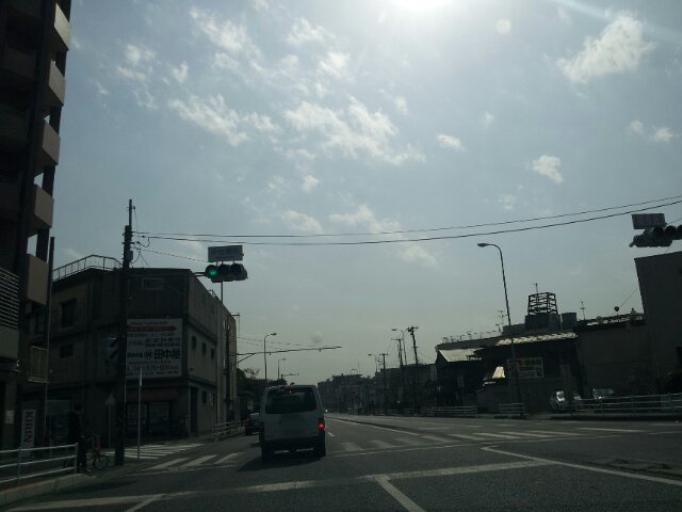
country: JP
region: Kanagawa
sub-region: Kawasaki-shi
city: Kawasaki
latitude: 35.5385
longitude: 139.6888
